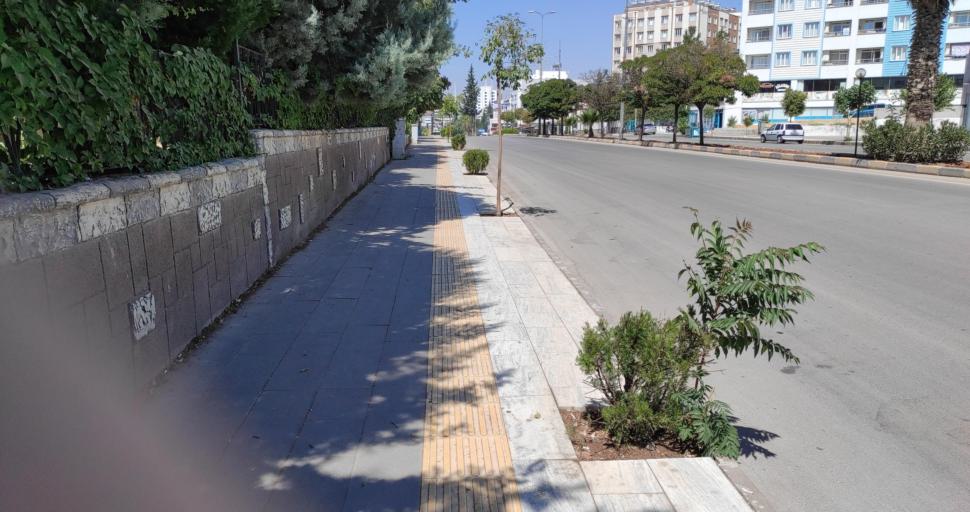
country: TR
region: Kilis
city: Kilis
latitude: 36.7262
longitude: 37.1023
